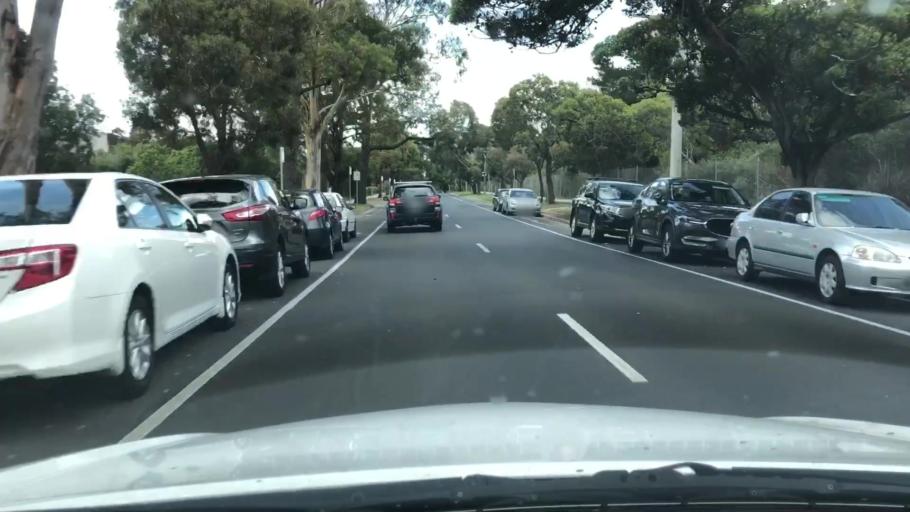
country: AU
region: Victoria
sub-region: Bayside
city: Highett
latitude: -37.9635
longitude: 145.0308
